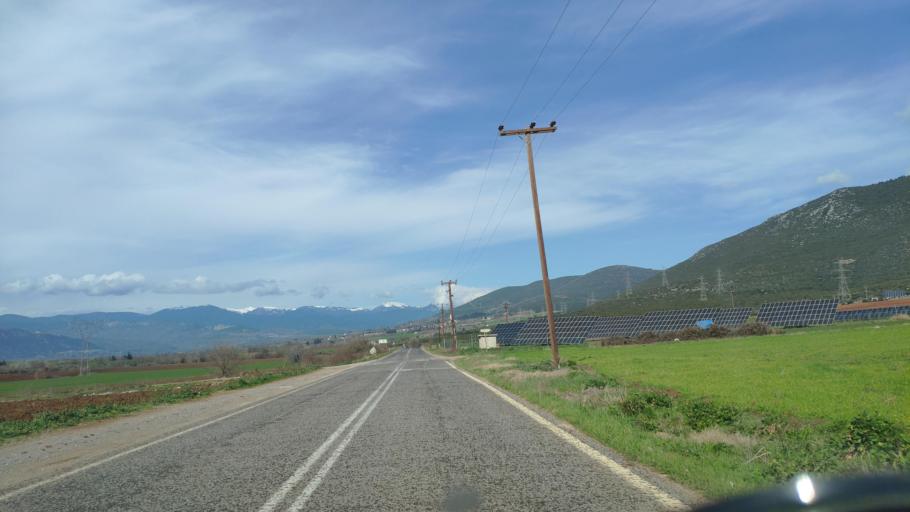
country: GR
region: Central Greece
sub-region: Nomos Fthiotidos
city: Amfikleia
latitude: 38.6954
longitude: 22.5239
